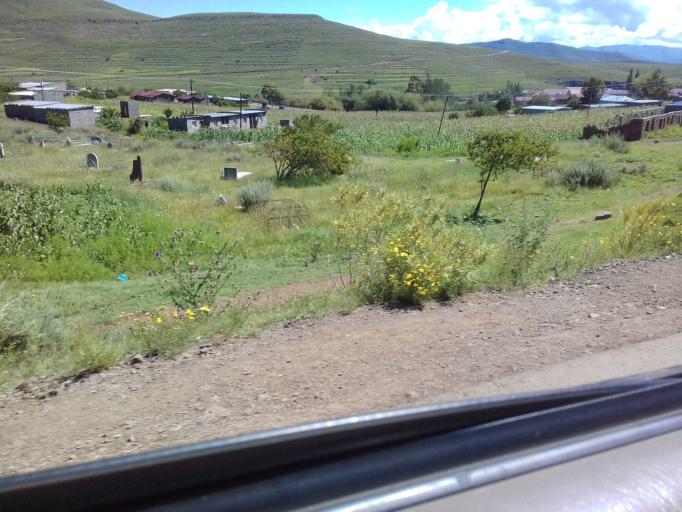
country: LS
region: Thaba-Tseka
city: Thaba-Tseka
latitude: -29.5149
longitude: 28.5967
